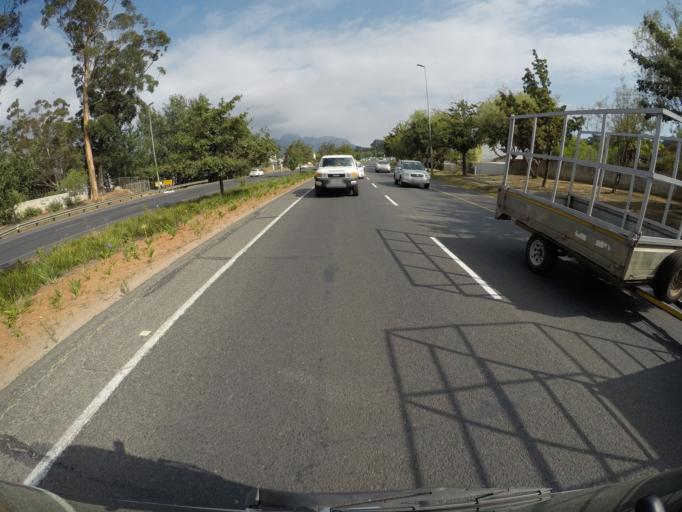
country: ZA
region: Western Cape
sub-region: Cape Winelands District Municipality
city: Stellenbosch
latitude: -33.9532
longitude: 18.8557
